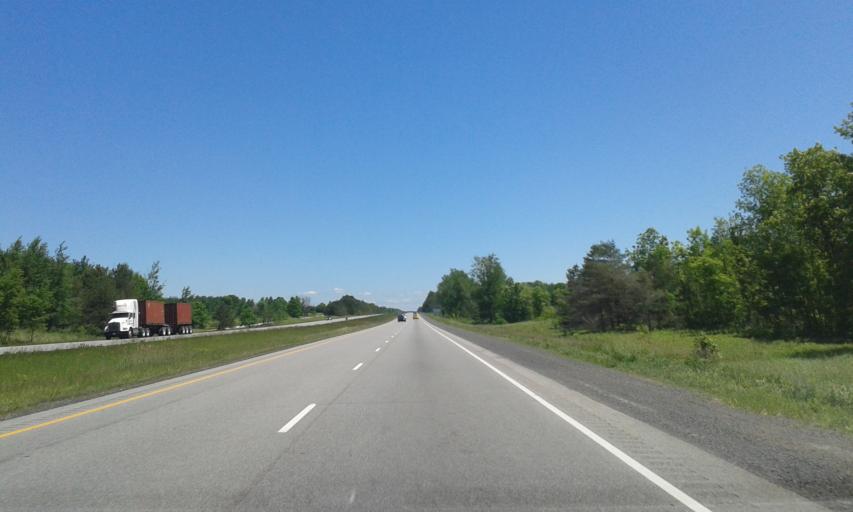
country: US
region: New York
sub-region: St. Lawrence County
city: Ogdensburg
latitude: 44.7974
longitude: -75.4261
